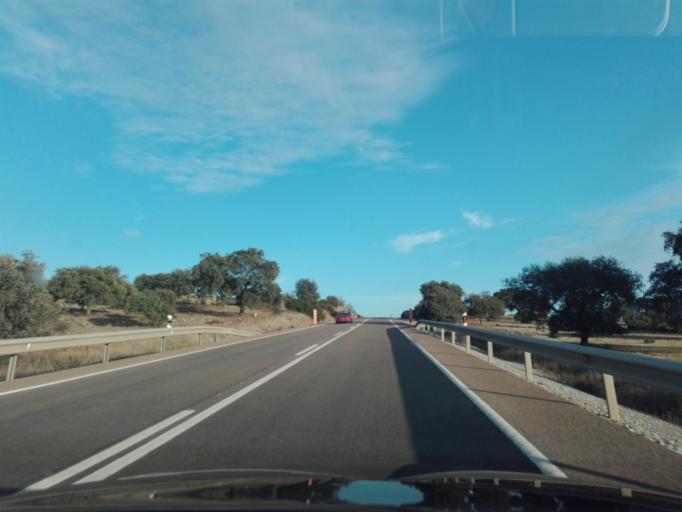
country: ES
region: Extremadura
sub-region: Provincia de Badajoz
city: Usagre
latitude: 38.3662
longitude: -6.2353
